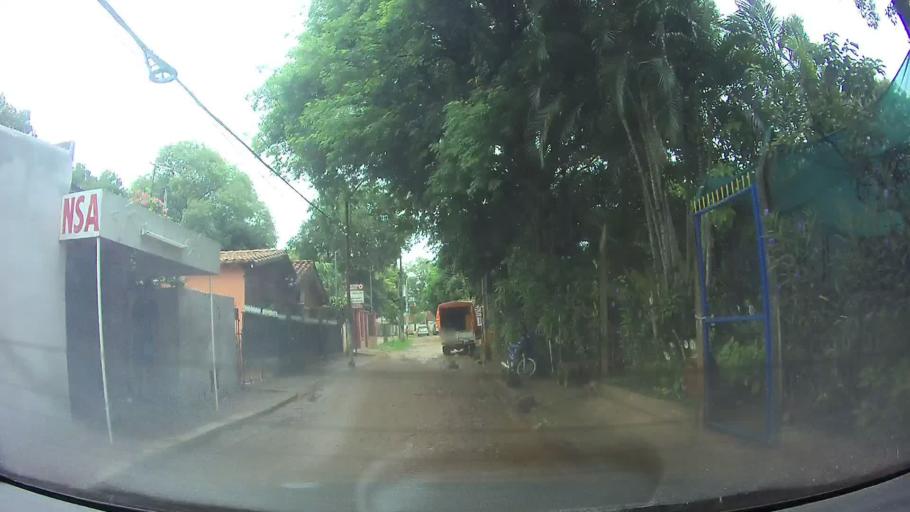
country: PY
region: Central
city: San Lorenzo
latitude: -25.2735
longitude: -57.4845
